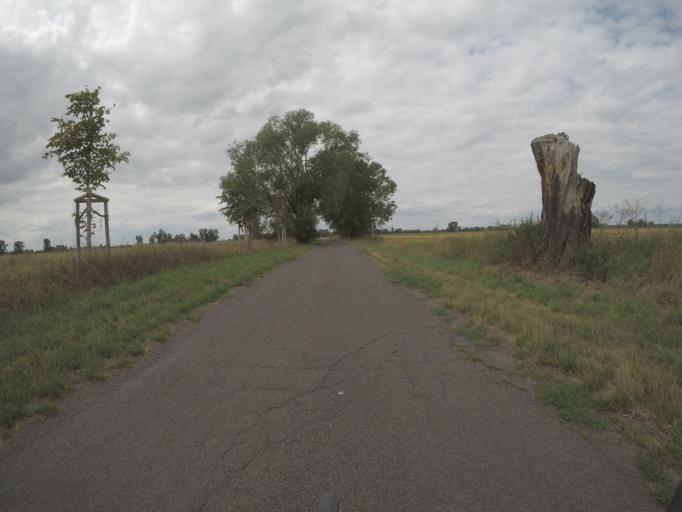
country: DE
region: Brandenburg
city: Wustermark
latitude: 52.6043
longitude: 12.9392
